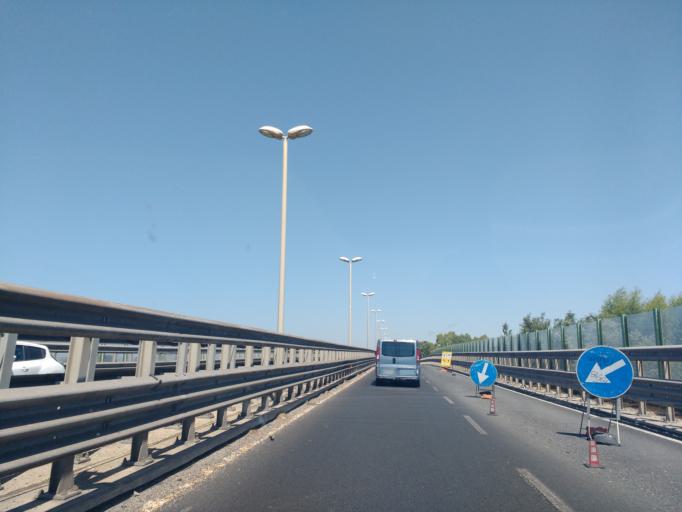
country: IT
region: Latium
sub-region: Citta metropolitana di Roma Capitale
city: Fiumicino-Isola Sacra
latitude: 41.7726
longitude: 12.2563
